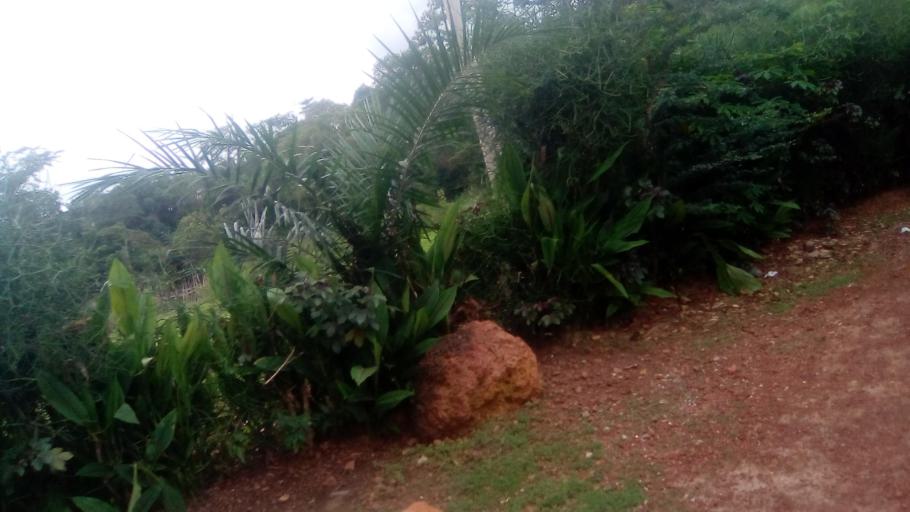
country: SL
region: Southern Province
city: Moyamba
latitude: 8.1559
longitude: -12.4260
